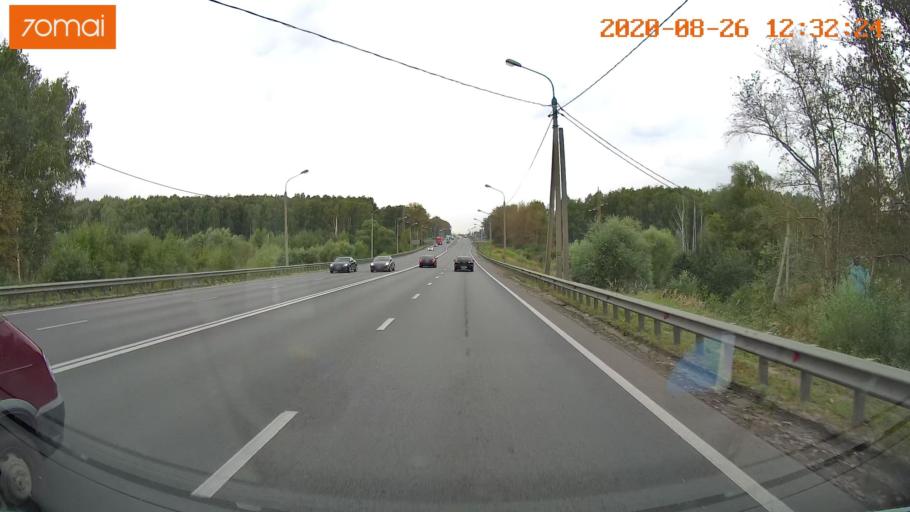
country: RU
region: Rjazan
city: Ryazan'
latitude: 54.5770
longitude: 39.7911
